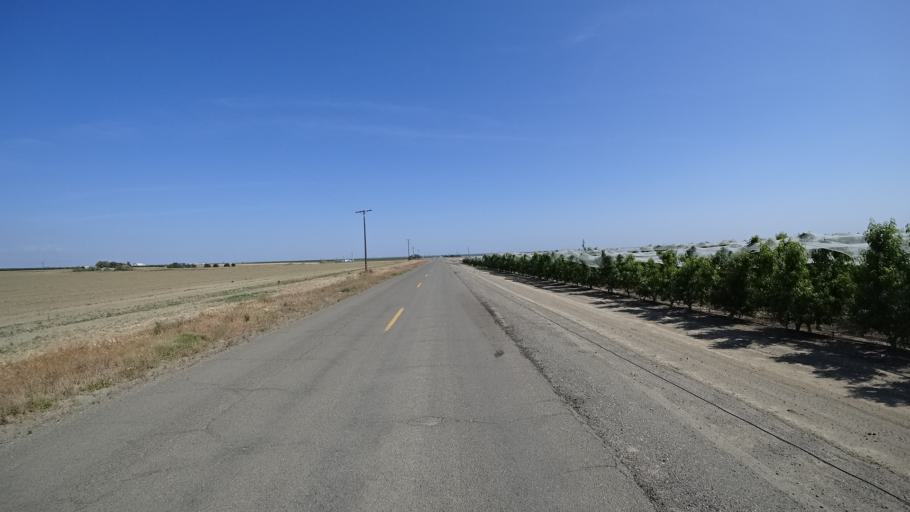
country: US
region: California
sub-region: Kings County
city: Kettleman City
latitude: 36.0445
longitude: -120.0033
